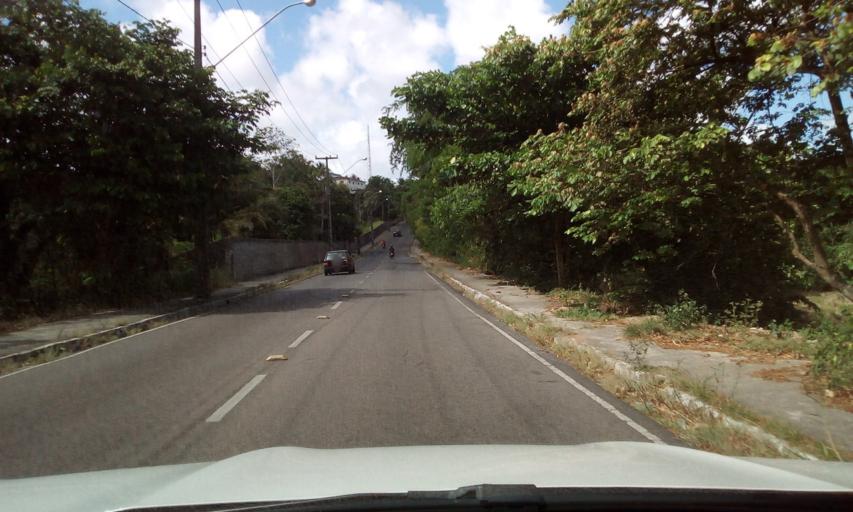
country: BR
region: Paraiba
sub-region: Joao Pessoa
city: Joao Pessoa
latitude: -7.1410
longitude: -34.8761
